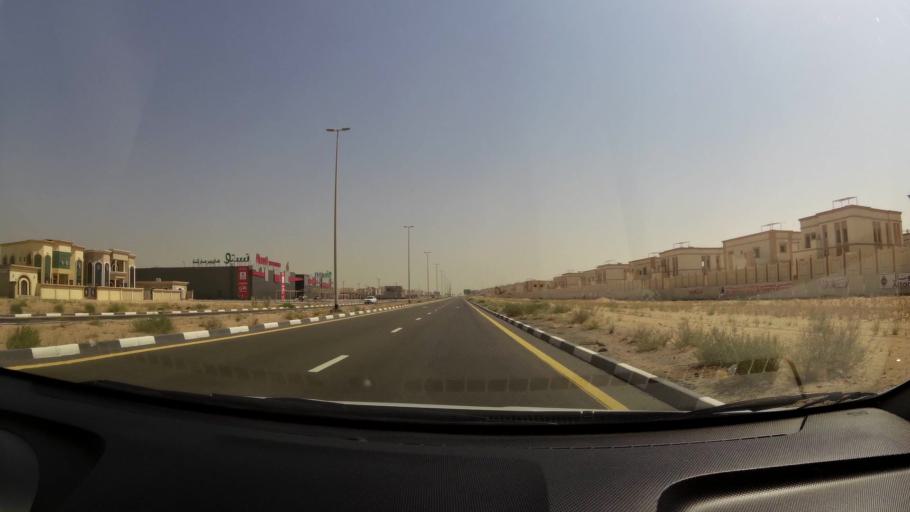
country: AE
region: Ajman
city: Ajman
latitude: 25.3967
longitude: 55.5491
